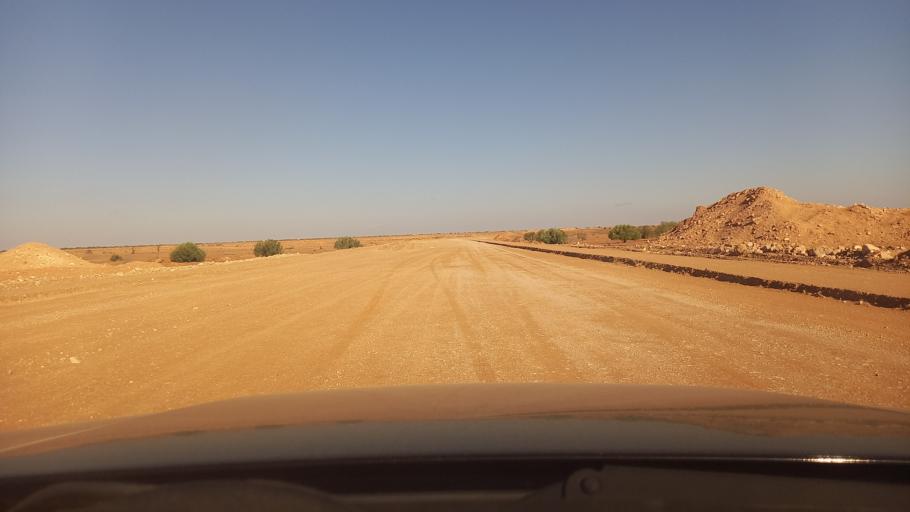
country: TN
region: Madanin
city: Medenine
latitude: 33.1430
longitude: 10.5060
